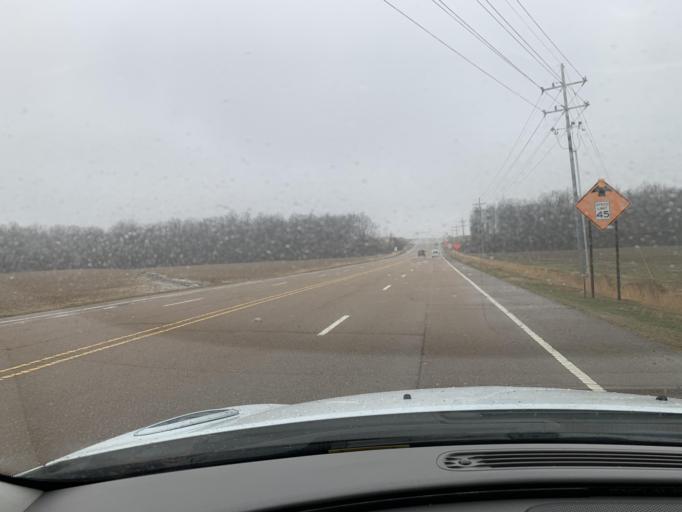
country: US
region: Mississippi
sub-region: De Soto County
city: Hernando
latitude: 34.8705
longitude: -89.9713
